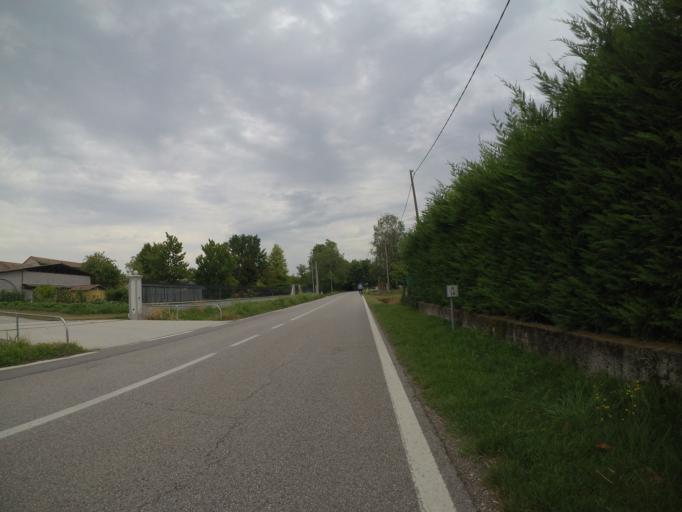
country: IT
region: Friuli Venezia Giulia
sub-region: Provincia di Udine
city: Varmo
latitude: 45.8943
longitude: 12.9774
